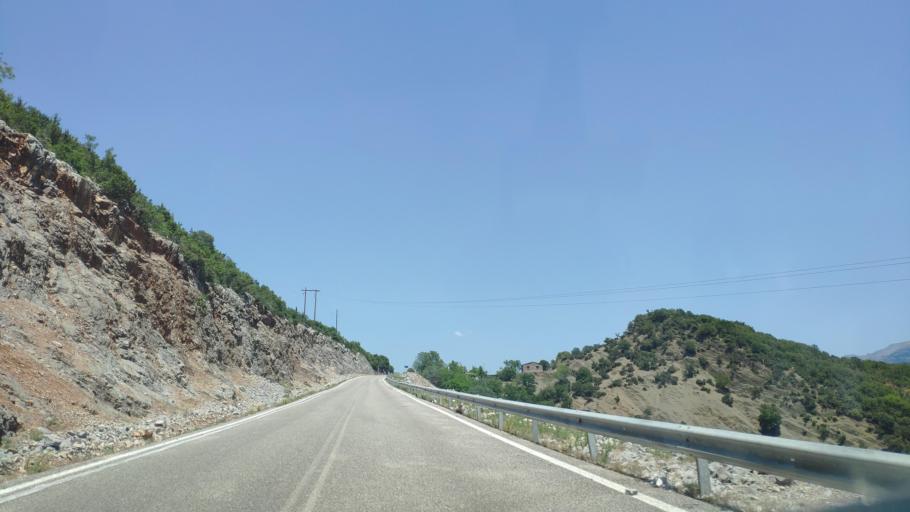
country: GR
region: Central Greece
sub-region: Nomos Evrytanias
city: Kerasochori
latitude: 39.1024
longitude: 21.4100
